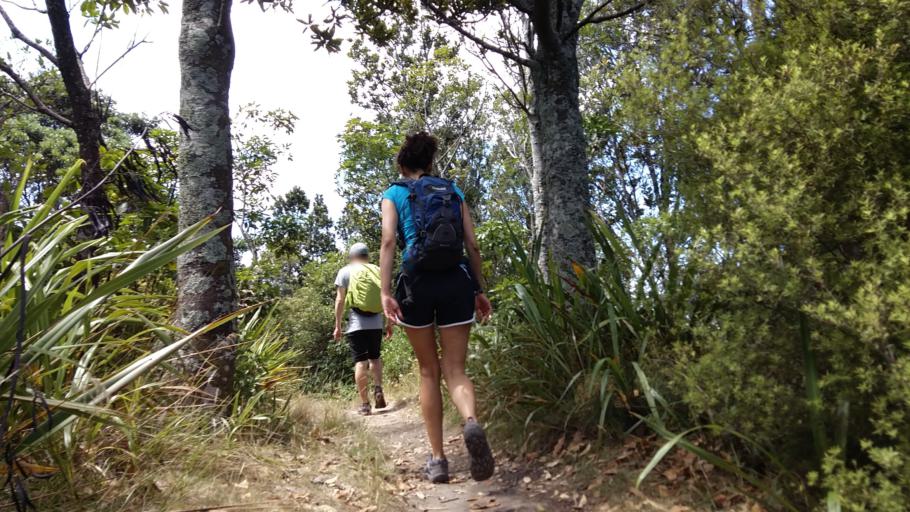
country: NZ
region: Bay of Plenty
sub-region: Whakatane District
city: Whakatane
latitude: -37.9480
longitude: 177.0114
